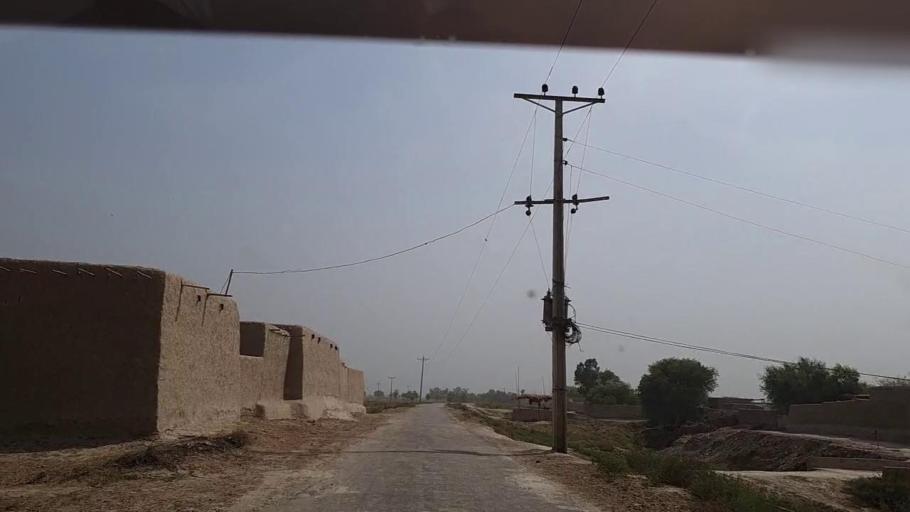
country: PK
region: Sindh
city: Khairpur Nathan Shah
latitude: 27.0386
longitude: 67.6851
